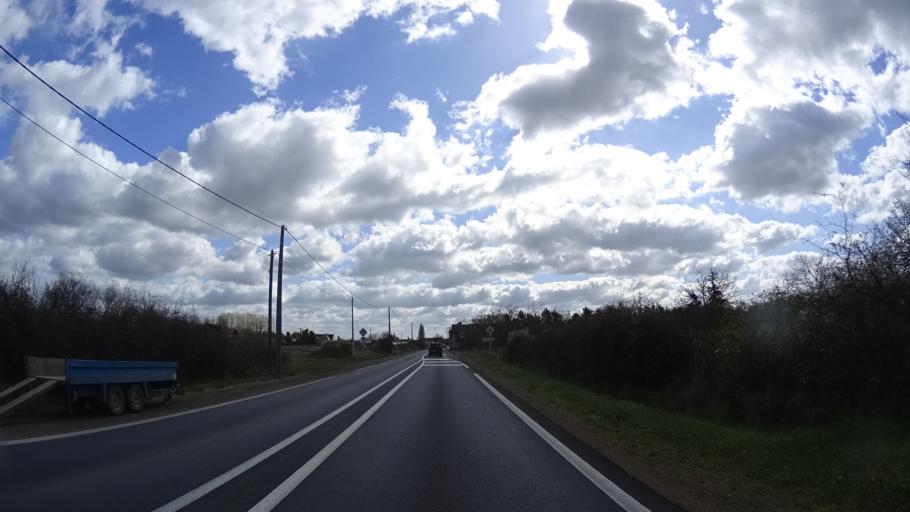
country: FR
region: Pays de la Loire
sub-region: Departement de Maine-et-Loire
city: Montreuil-Bellay
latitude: 47.0995
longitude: -0.0937
